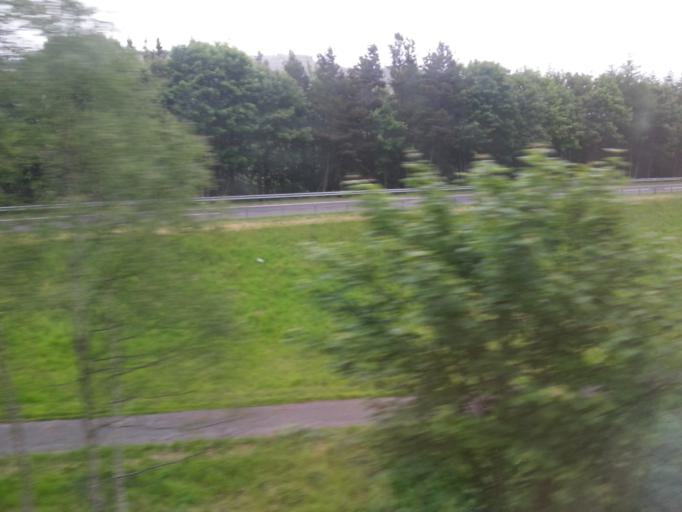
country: GB
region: Scotland
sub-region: Perth and Kinross
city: Bankfoot
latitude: 56.5532
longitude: -3.5671
